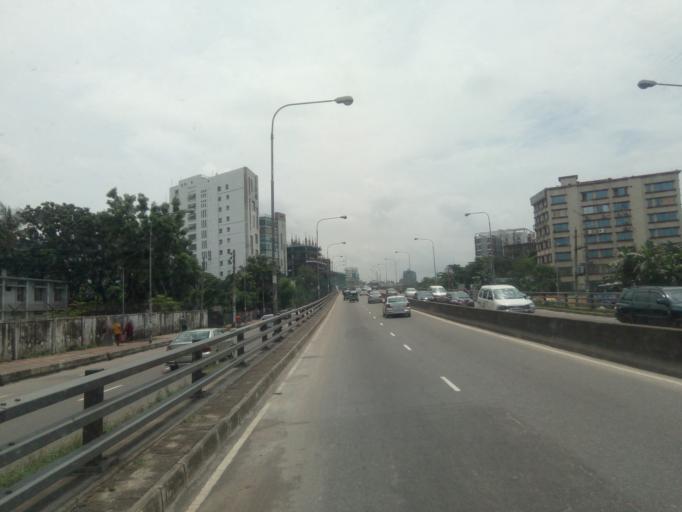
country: BD
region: Dhaka
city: Paltan
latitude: 23.7766
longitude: 90.3942
